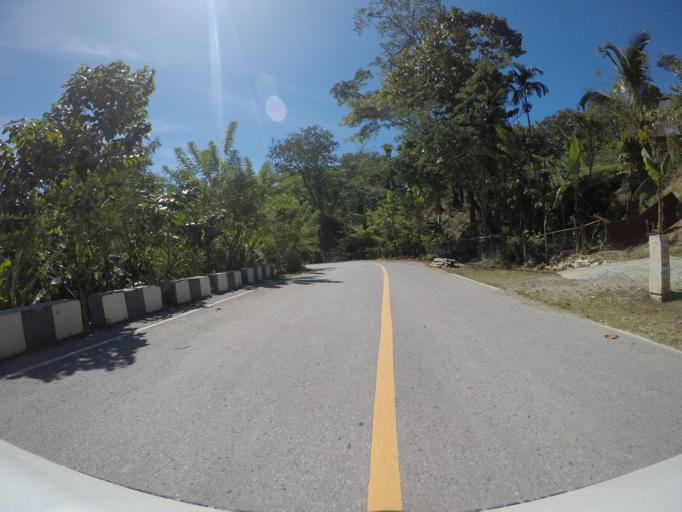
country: TL
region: Manufahi
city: Same
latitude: -8.9108
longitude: 125.9740
